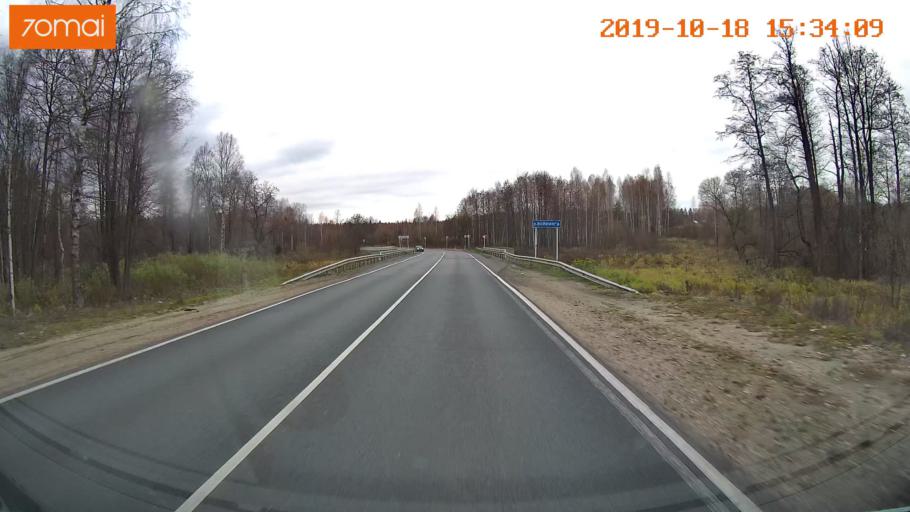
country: RU
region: Vladimir
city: Anopino
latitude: 55.8514
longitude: 40.6450
